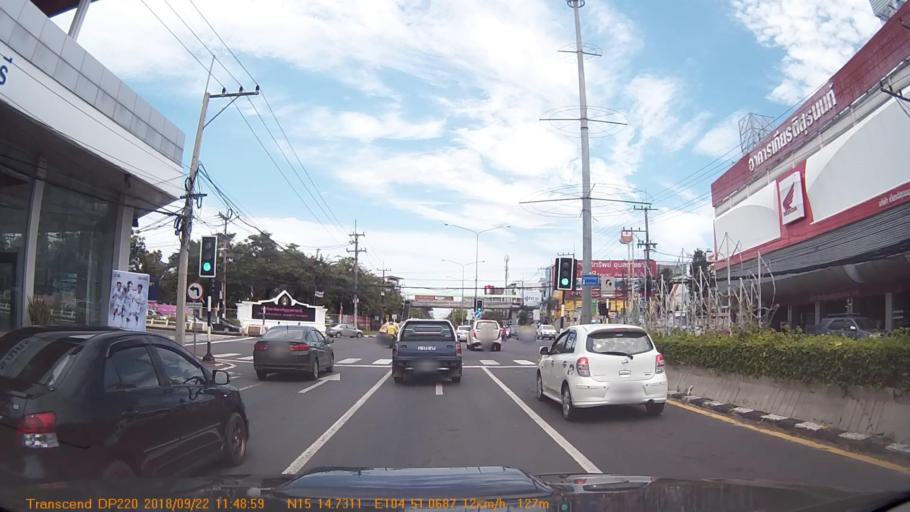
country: TH
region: Changwat Ubon Ratchathani
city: Ubon Ratchathani
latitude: 15.2449
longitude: 104.8514
